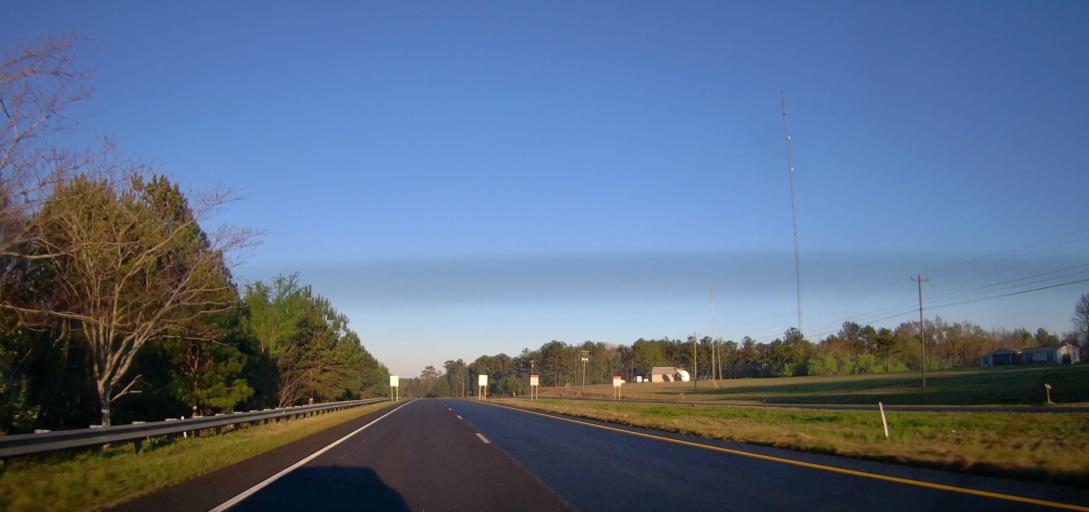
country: US
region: Georgia
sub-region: Wilkinson County
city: Gordon
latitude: 32.8502
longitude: -83.4767
